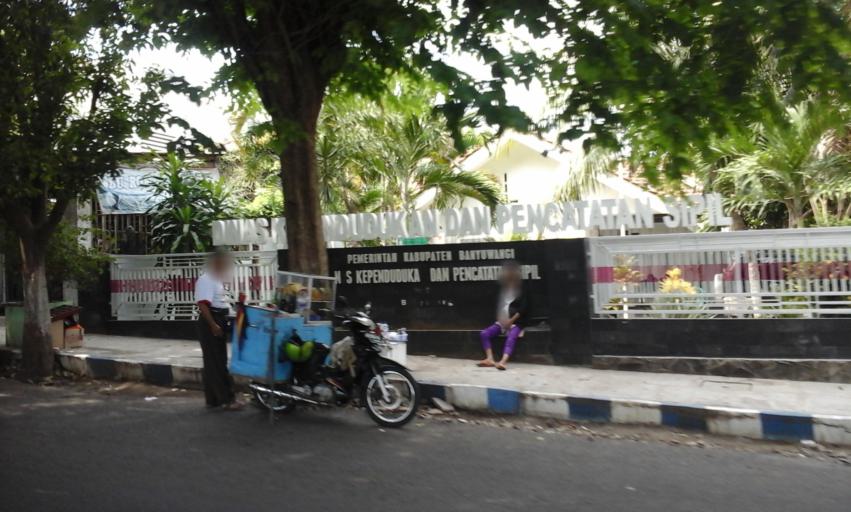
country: ID
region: East Java
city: Wirodayan
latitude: -8.2077
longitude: 114.3649
